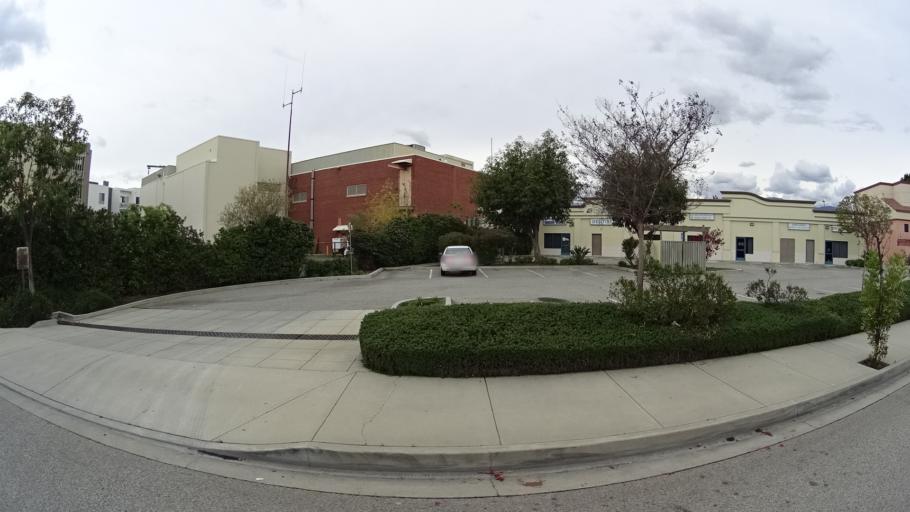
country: US
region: California
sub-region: Los Angeles County
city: Baldwin Park
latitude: 34.0861
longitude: -117.9581
